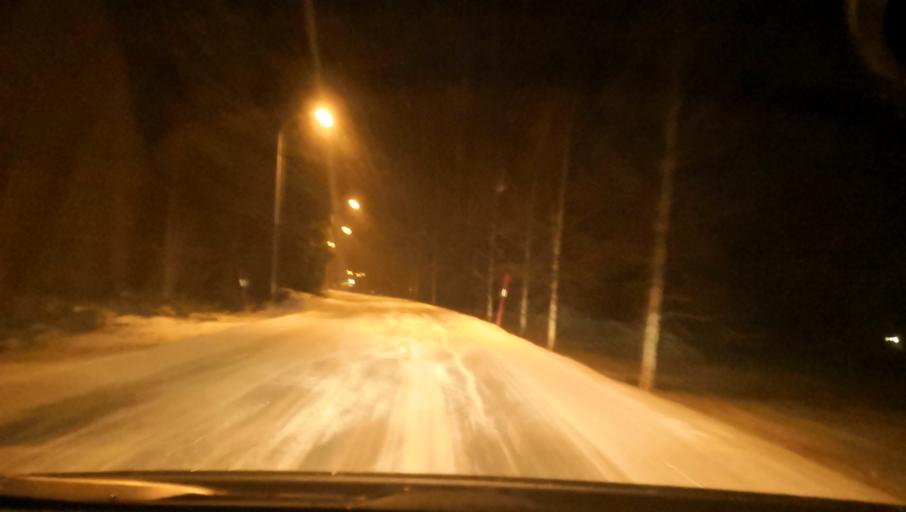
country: SE
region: Uppsala
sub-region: Heby Kommun
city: Tarnsjo
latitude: 60.1470
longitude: 16.9160
